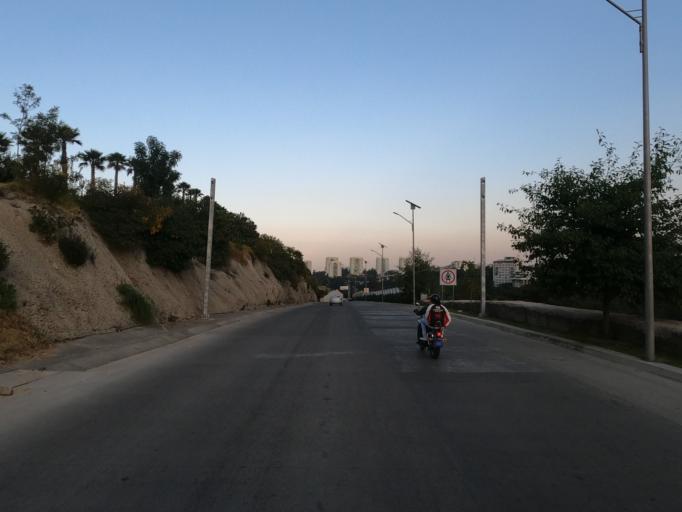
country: MX
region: Mexico
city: San Bartolome Coatepec
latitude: 19.4128
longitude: -99.2910
